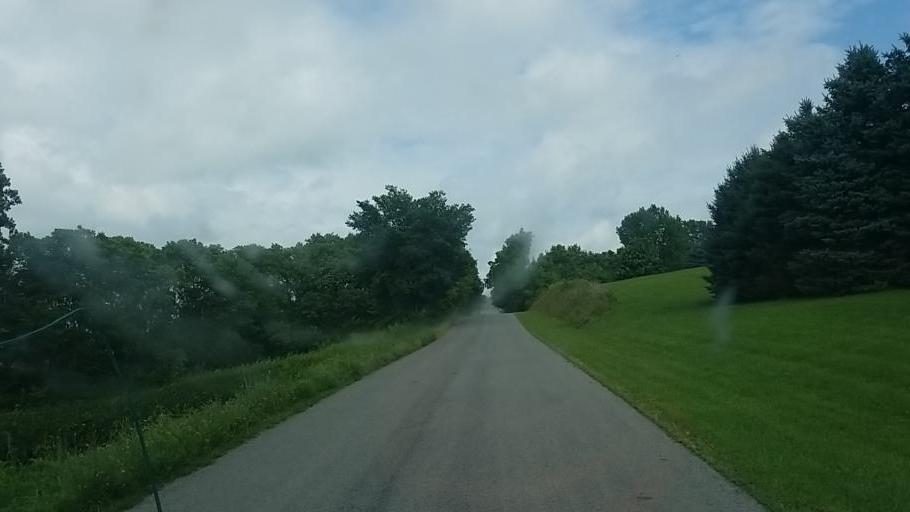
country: US
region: Ohio
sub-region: Champaign County
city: North Lewisburg
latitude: 40.2576
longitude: -83.6318
